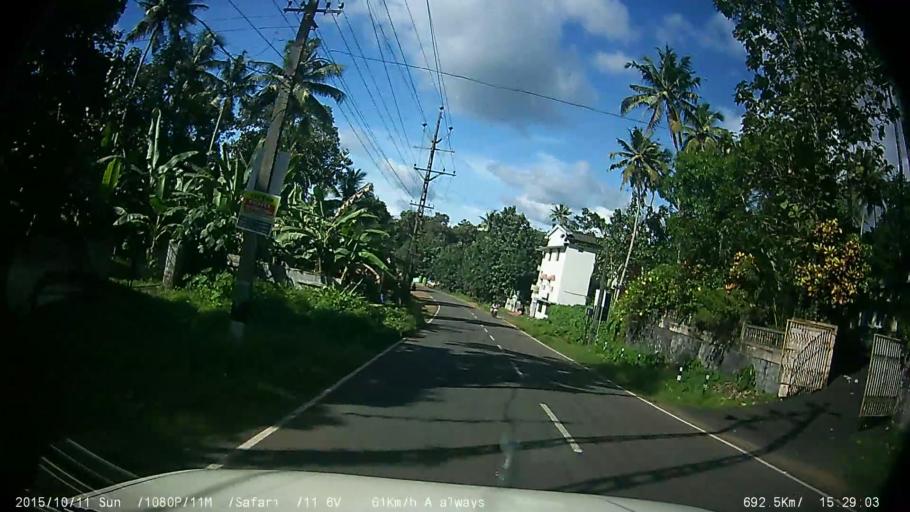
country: IN
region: Kerala
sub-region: Kottayam
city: Changanacheri
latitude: 9.4934
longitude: 76.5729
